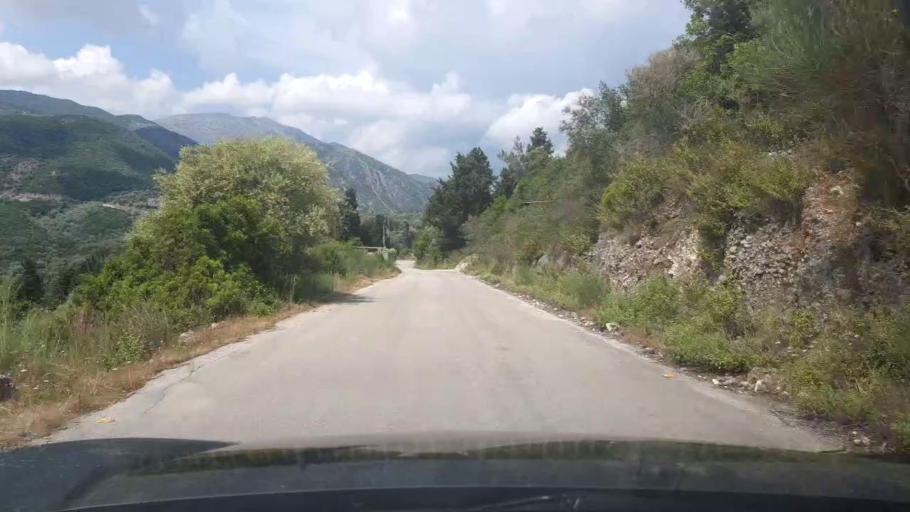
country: GR
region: Ionian Islands
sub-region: Lefkada
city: Nidri
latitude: 38.6470
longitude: 20.7046
